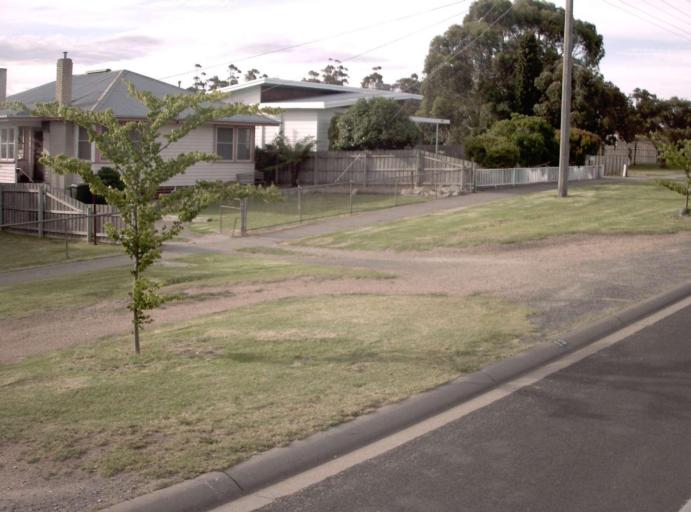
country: AU
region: Victoria
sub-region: Wellington
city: Sale
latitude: -37.9688
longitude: 146.9845
